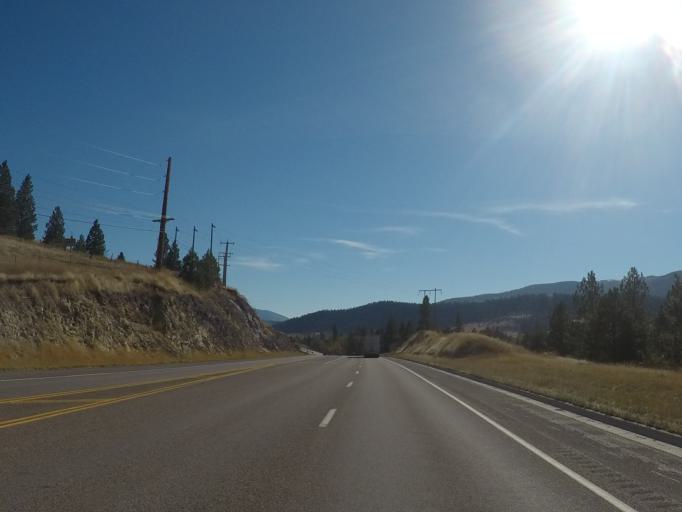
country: US
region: Montana
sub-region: Missoula County
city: Frenchtown
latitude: 47.1824
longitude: -114.1013
